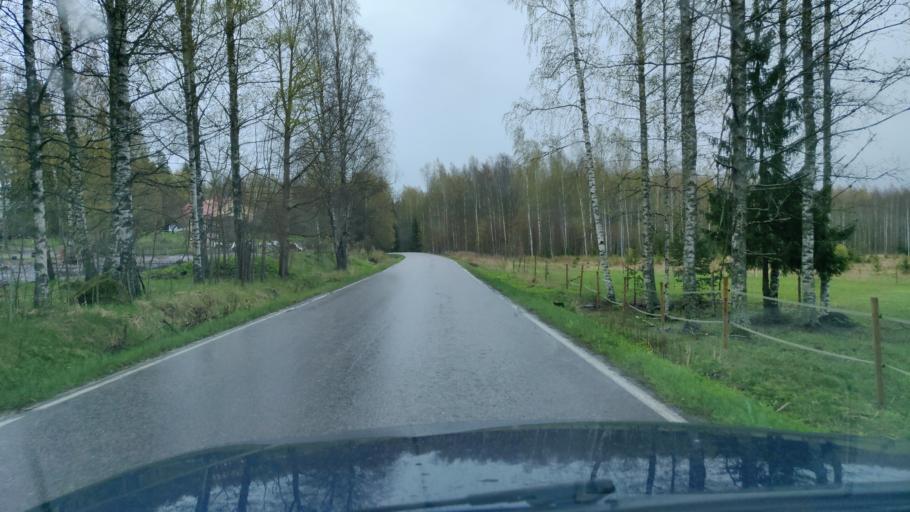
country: FI
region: Uusimaa
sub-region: Helsinki
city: Nurmijaervi
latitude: 60.4993
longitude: 24.7015
